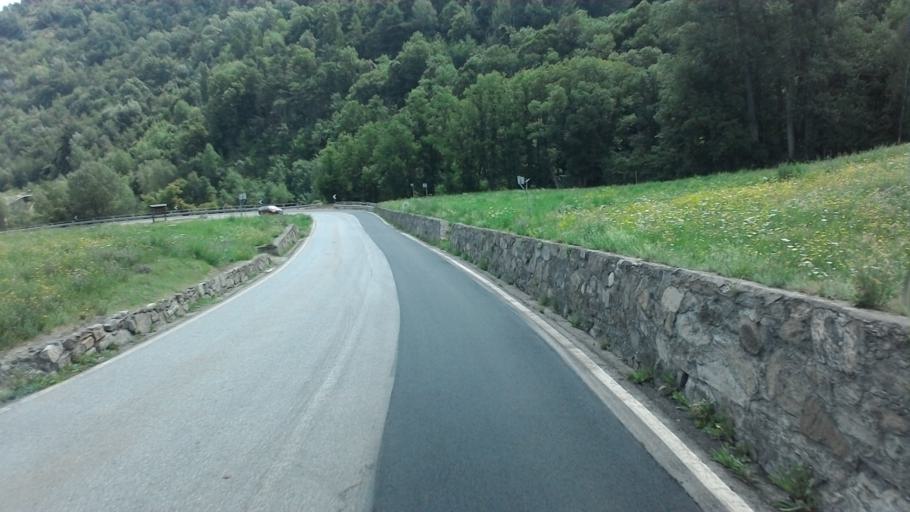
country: IT
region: Aosta Valley
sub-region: Valle d'Aosta
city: Plan d'Introd
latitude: 45.6959
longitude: 7.1935
